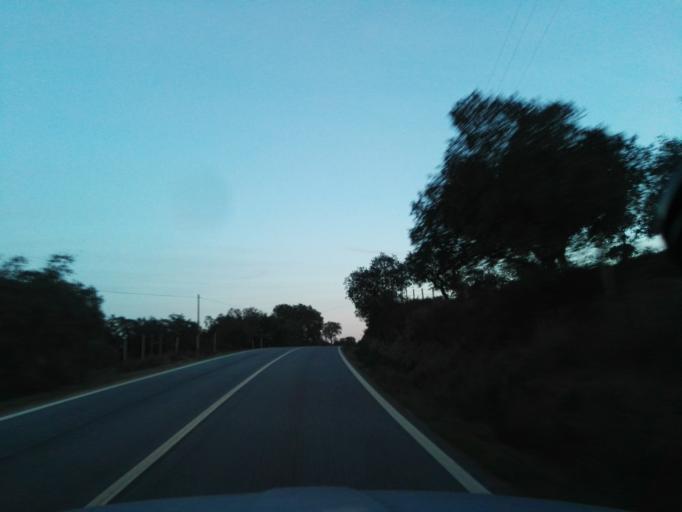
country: PT
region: Evora
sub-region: Arraiolos
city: Arraiolos
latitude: 38.7515
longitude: -8.0922
